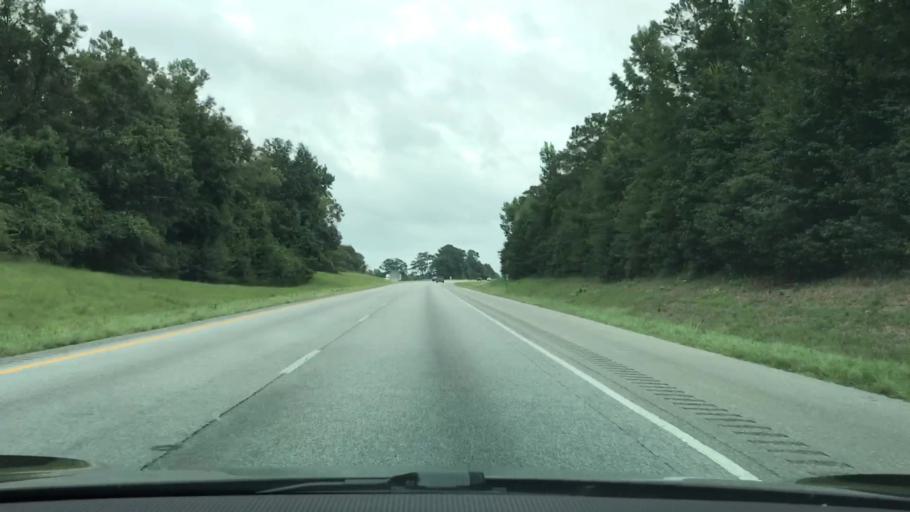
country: US
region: Alabama
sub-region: Lee County
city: Auburn
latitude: 32.5248
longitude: -85.5707
